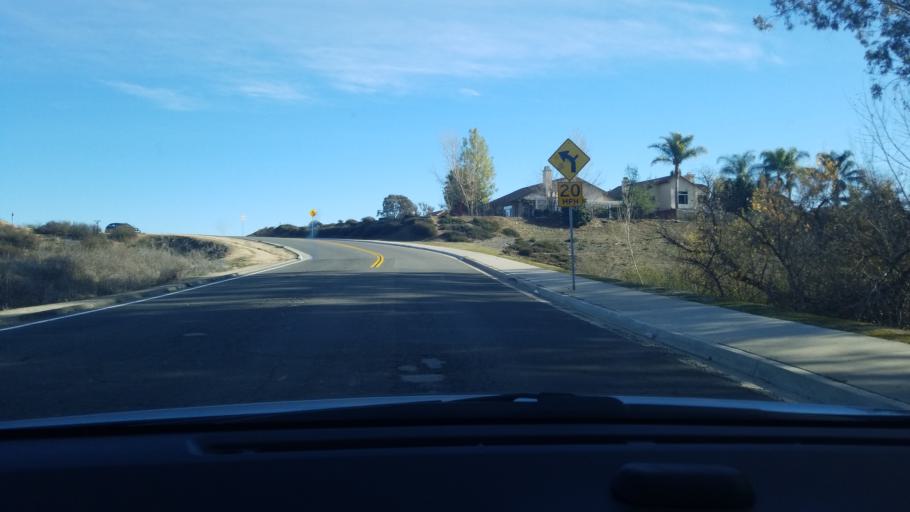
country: US
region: California
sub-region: Riverside County
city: Murrieta
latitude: 33.5663
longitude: -117.1926
